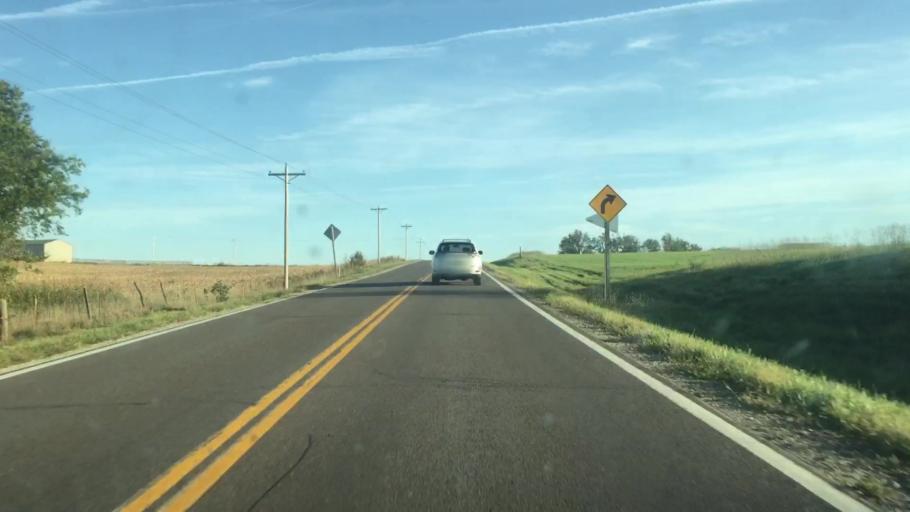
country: US
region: Kansas
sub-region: Brown County
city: Horton
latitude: 39.5678
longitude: -95.5258
